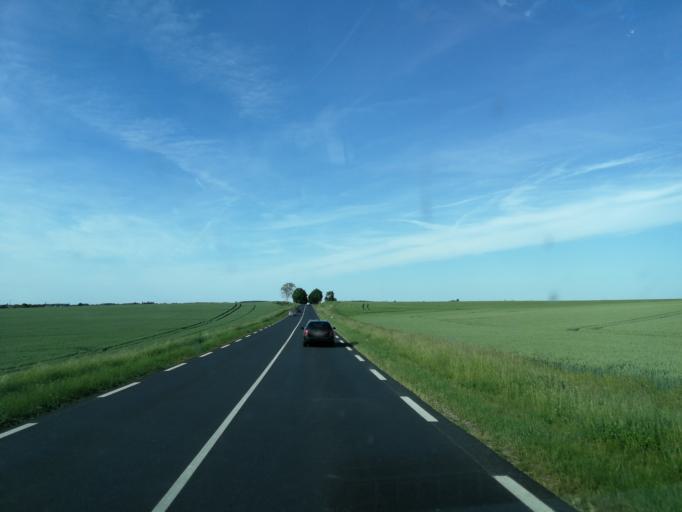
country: FR
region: Centre
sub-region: Departement du Loir-et-Cher
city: Saint-Amand-Longpre
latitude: 47.7359
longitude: 1.0314
